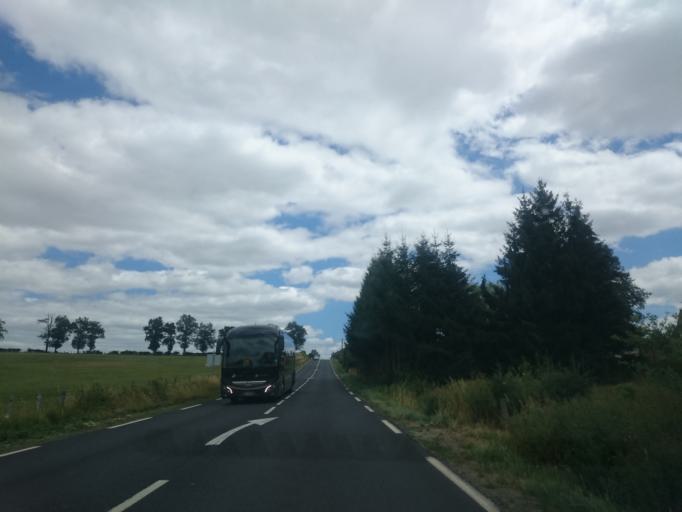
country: FR
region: Auvergne
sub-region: Departement du Cantal
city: Saint-Paul-des-Landes
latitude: 44.9531
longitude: 2.2858
